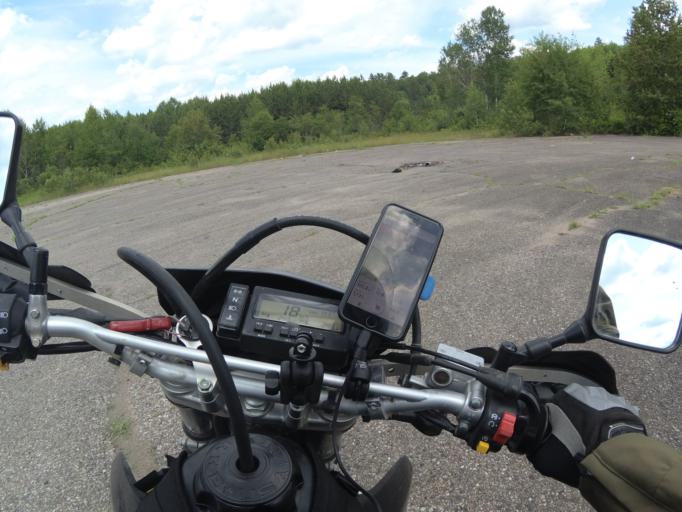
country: CA
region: Ontario
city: Bancroft
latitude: 45.0321
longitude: -77.2668
